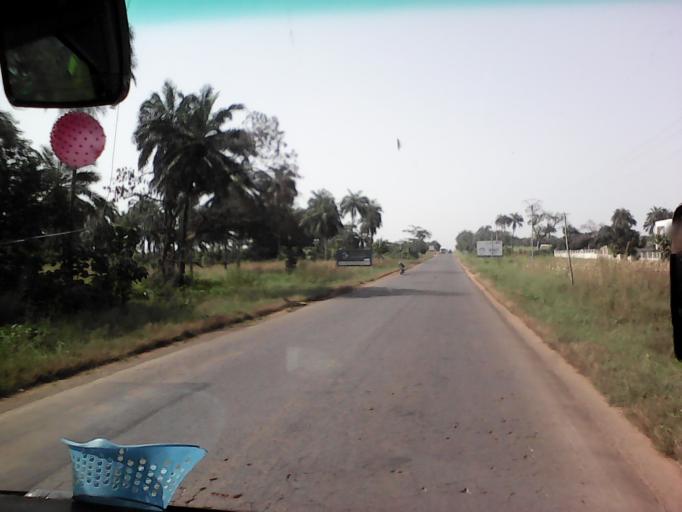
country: TG
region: Centrale
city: Sokode
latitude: 8.9581
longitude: 1.1357
